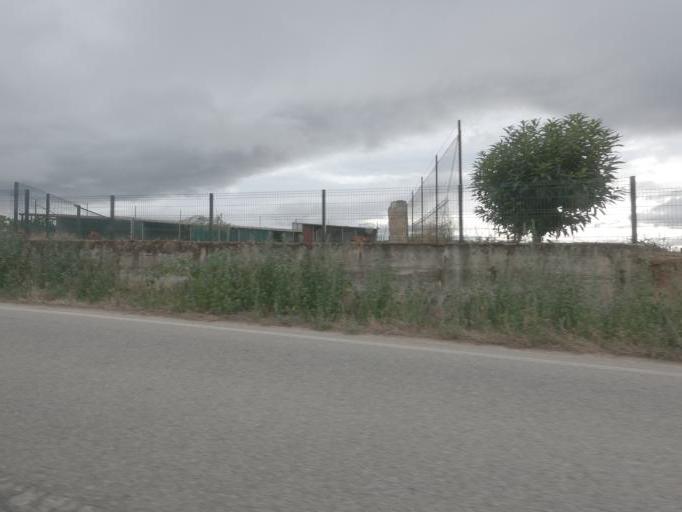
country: PT
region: Vila Real
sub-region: Sabrosa
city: Sabrosa
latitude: 41.2804
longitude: -7.5125
